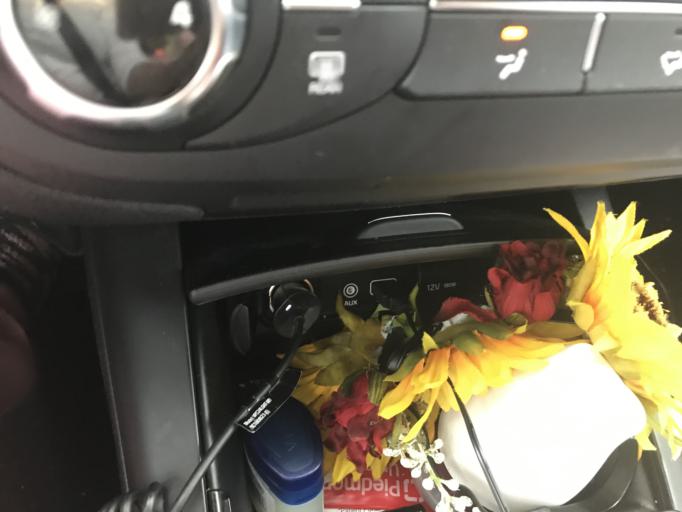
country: US
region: Georgia
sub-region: Cobb County
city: Mableton
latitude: 33.7886
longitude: -84.5475
